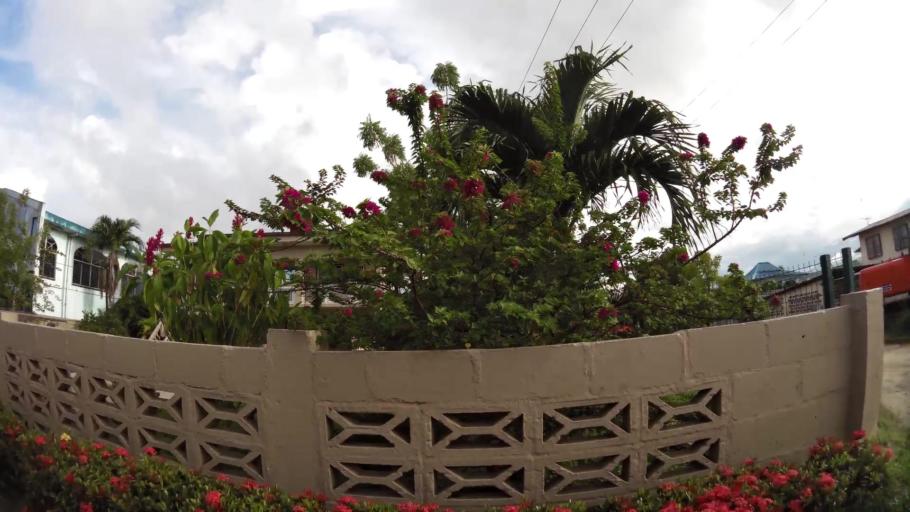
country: SR
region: Paramaribo
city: Paramaribo
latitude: 5.8473
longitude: -55.2390
